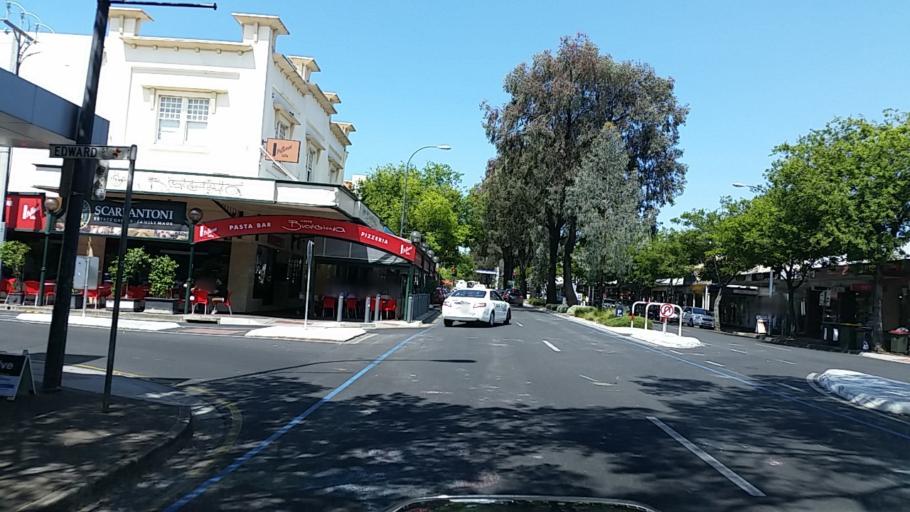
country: AU
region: South Australia
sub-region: Norwood Payneham St Peters
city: Trinity Gardens
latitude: -34.9212
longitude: 138.6342
